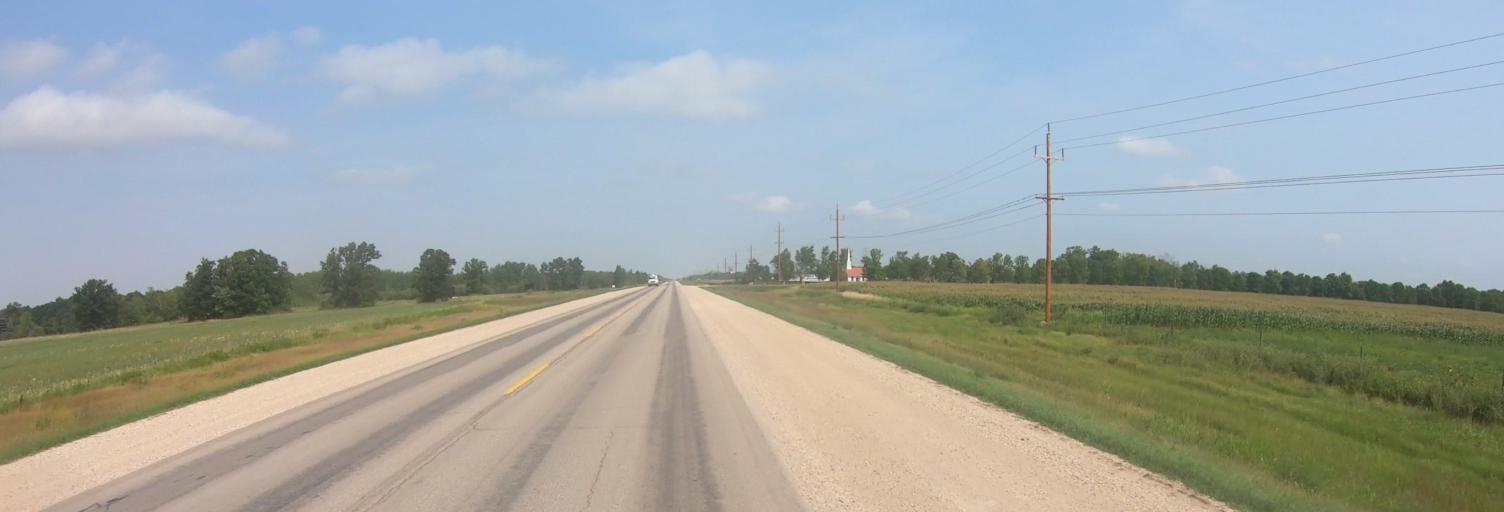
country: CA
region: Manitoba
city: Steinbach
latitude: 49.4775
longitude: -96.6910
